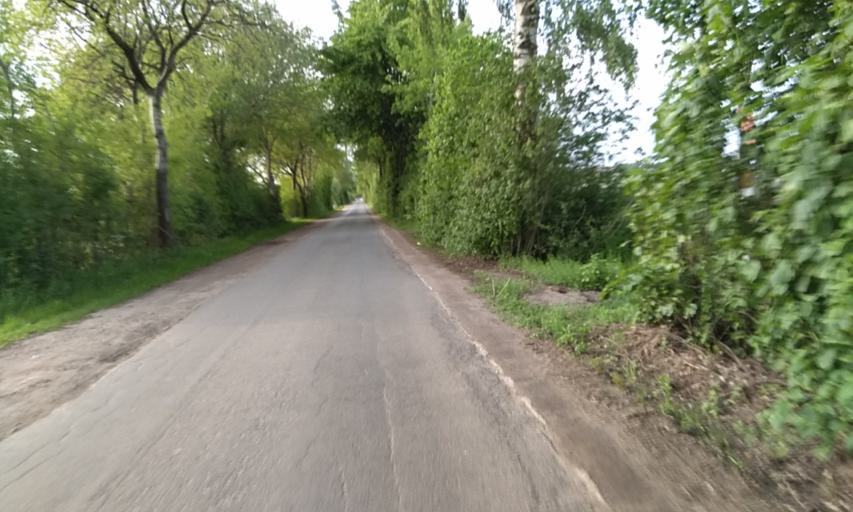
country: DE
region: Lower Saxony
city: Harsefeld
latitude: 53.4361
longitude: 9.4970
